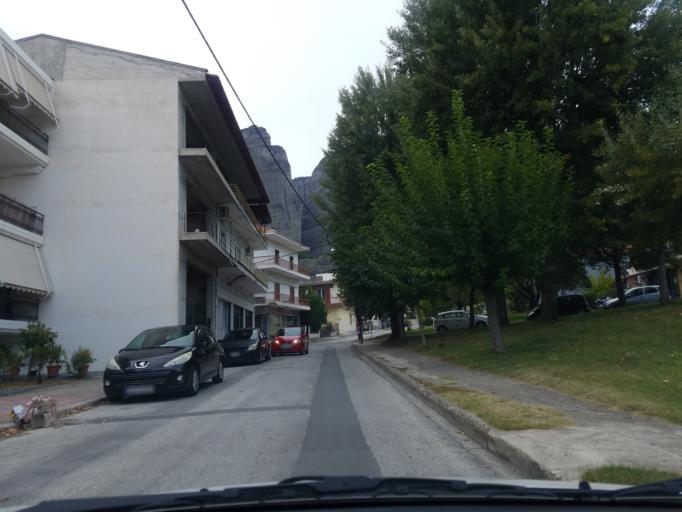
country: GR
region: Thessaly
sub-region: Trikala
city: Kalampaka
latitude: 39.7061
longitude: 21.6303
